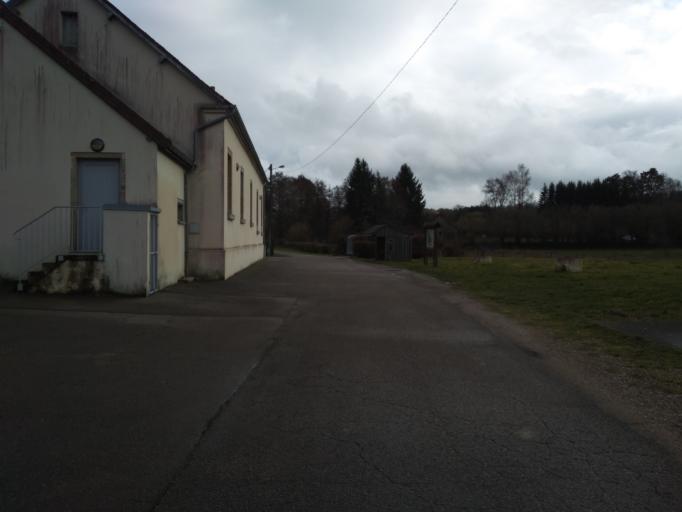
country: FR
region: Bourgogne
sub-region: Departement de la Cote-d'Or
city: Saulieu
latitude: 47.2768
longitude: 4.1419
